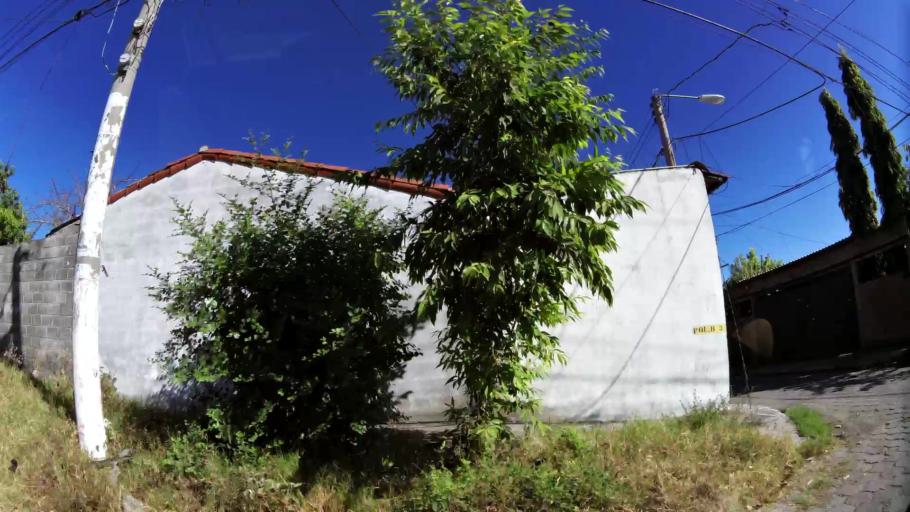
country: SV
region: San Miguel
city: San Miguel
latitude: 13.4705
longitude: -88.1565
